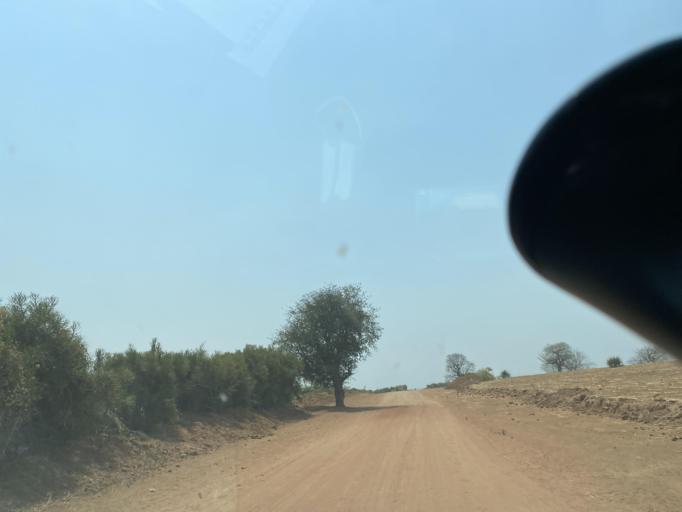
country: ZW
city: Chirundu
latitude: -16.1514
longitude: 28.8017
